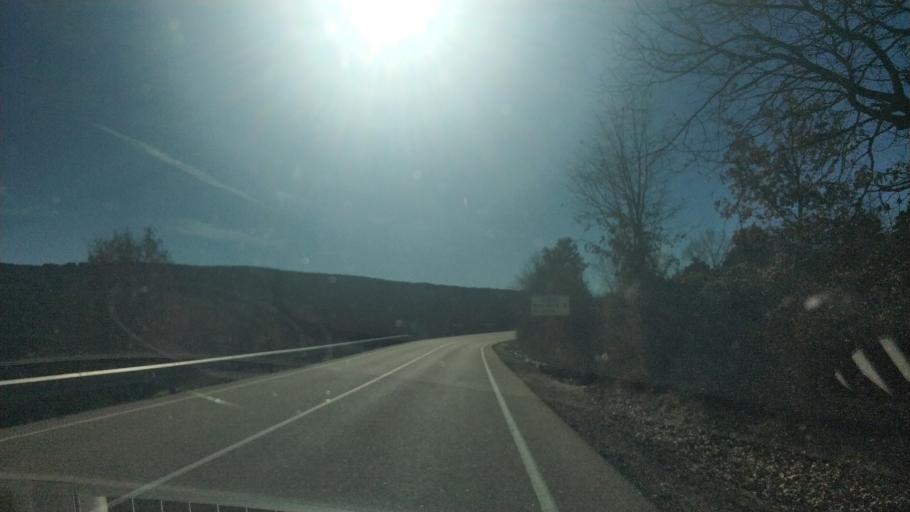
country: ES
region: Castille and Leon
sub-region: Provincia de Soria
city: Vinuesa
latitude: 41.9032
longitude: -2.7663
